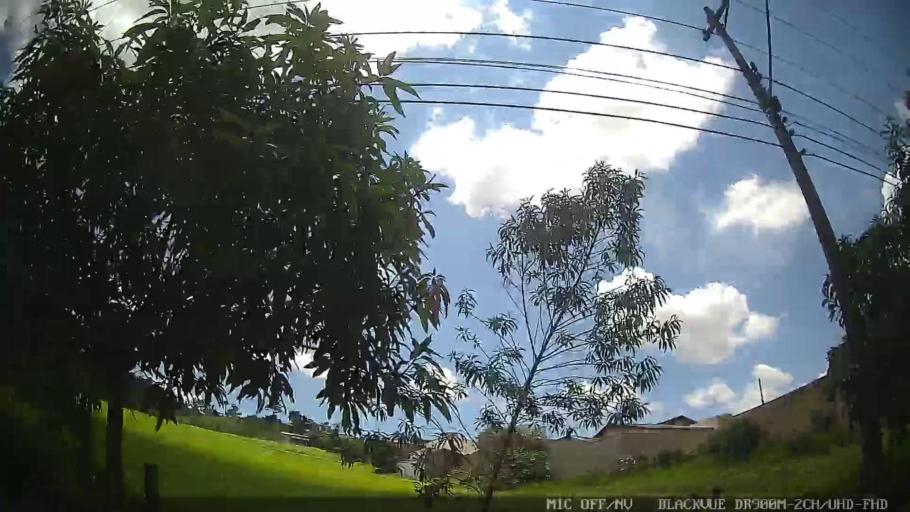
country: BR
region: Sao Paulo
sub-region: Itatiba
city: Itatiba
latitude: -22.8728
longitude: -46.7901
